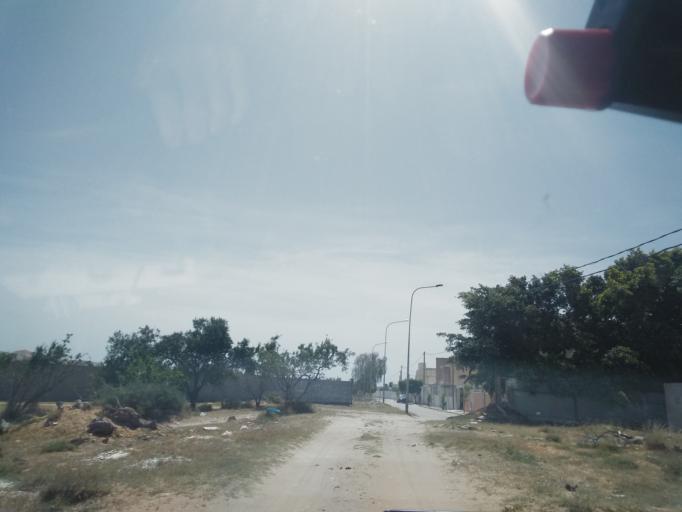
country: TN
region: Safaqis
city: Al Qarmadah
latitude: 34.8052
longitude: 10.7717
